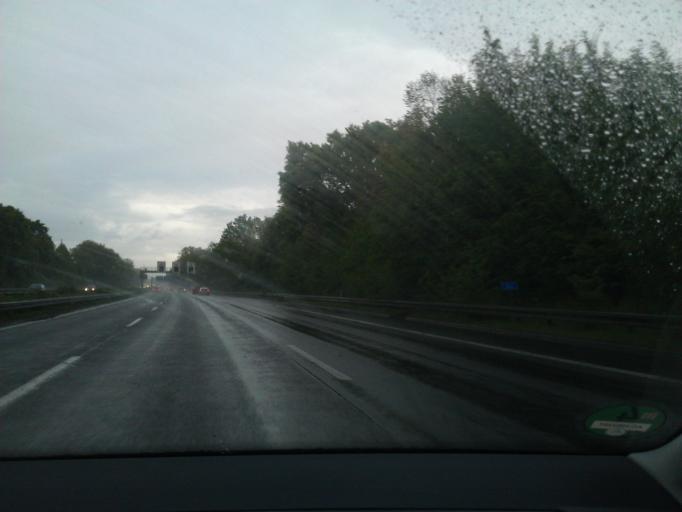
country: DE
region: North Rhine-Westphalia
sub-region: Regierungsbezirk Koln
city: Bayenthal
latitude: 50.8702
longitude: 6.9700
